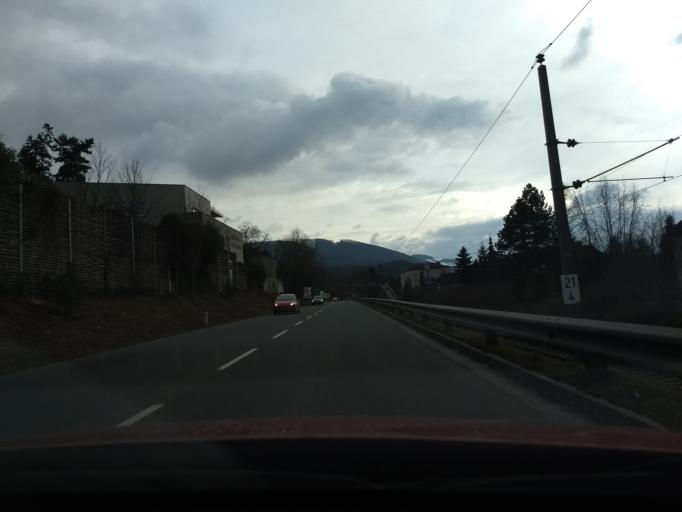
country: AT
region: Upper Austria
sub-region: Politischer Bezirk Steyr-Land
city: Sankt Ulrich bei Steyr
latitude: 48.0306
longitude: 14.4188
